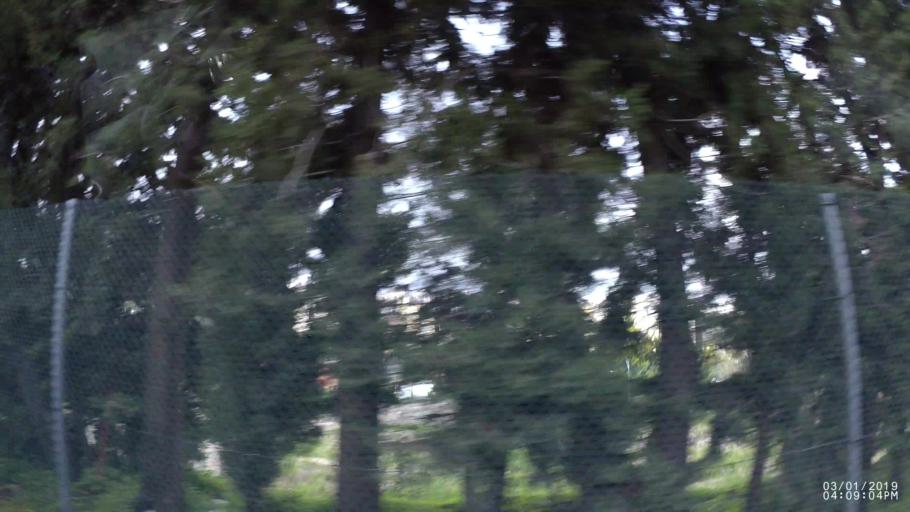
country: JO
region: Amman
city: Al Bunayyat ash Shamaliyah
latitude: 31.9534
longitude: 35.8833
